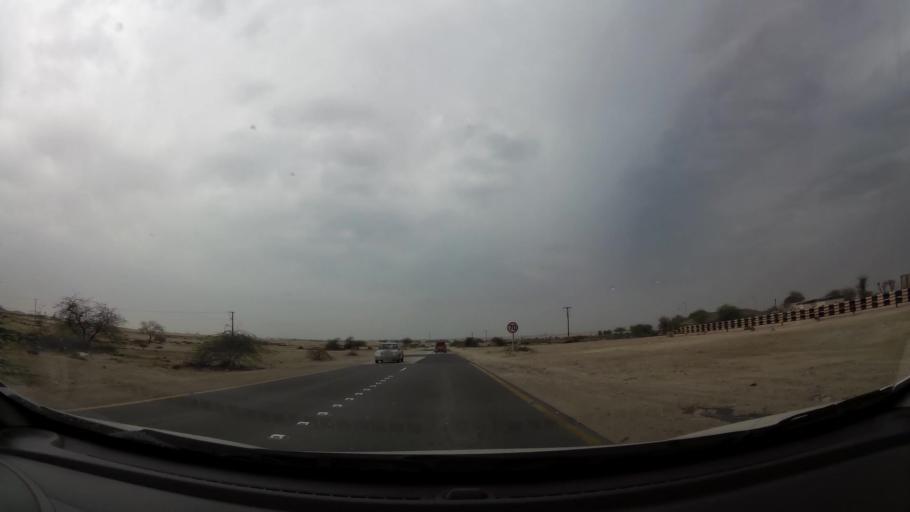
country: BH
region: Central Governorate
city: Dar Kulayb
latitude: 26.0790
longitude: 50.5483
